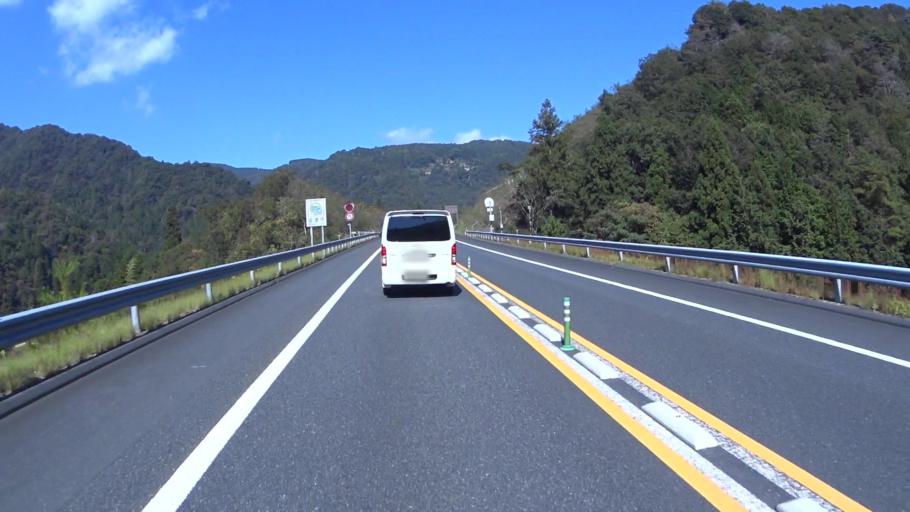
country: JP
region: Kyoto
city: Miyazu
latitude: 35.4608
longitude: 135.1740
